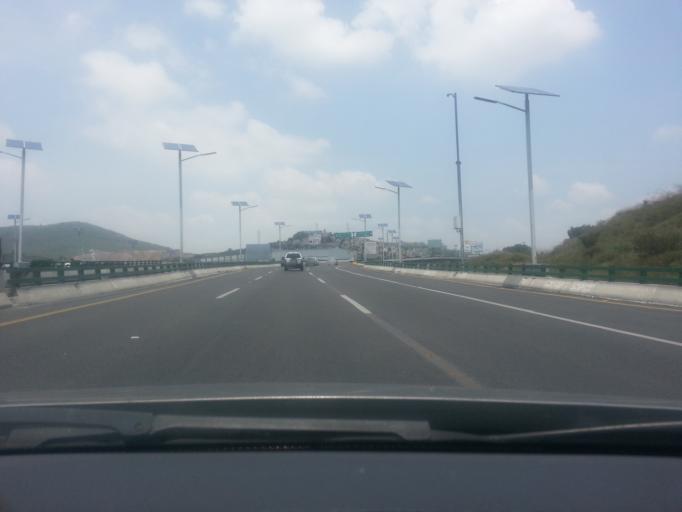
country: MX
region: Mexico
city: Tlalnepantla
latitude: 19.5745
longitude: -99.2081
